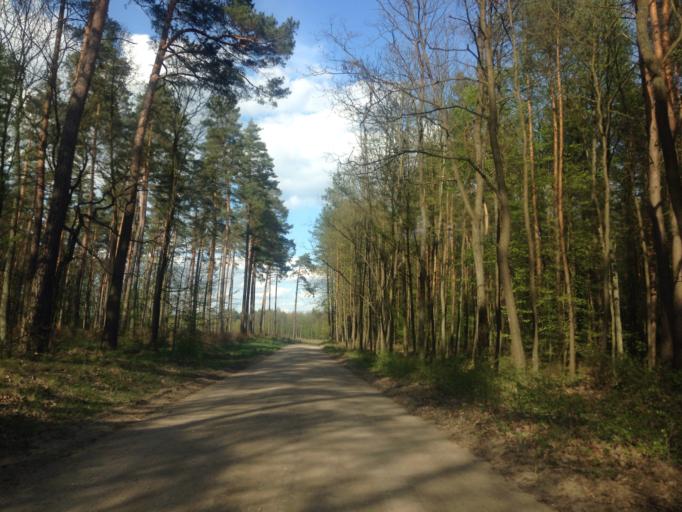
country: PL
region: Kujawsko-Pomorskie
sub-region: Powiat brodnicki
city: Gorzno
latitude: 53.2034
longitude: 19.7099
